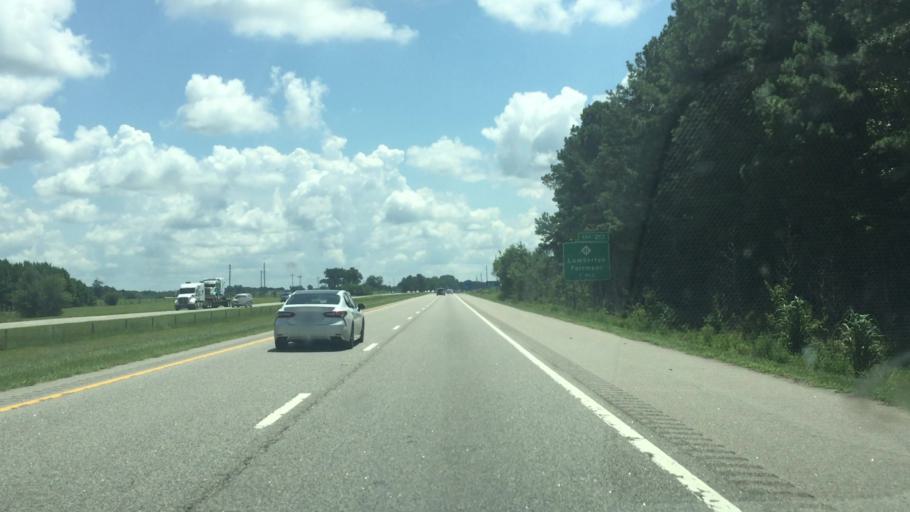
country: US
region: North Carolina
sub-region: Robeson County
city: Lumberton
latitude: 34.5894
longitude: -79.0675
